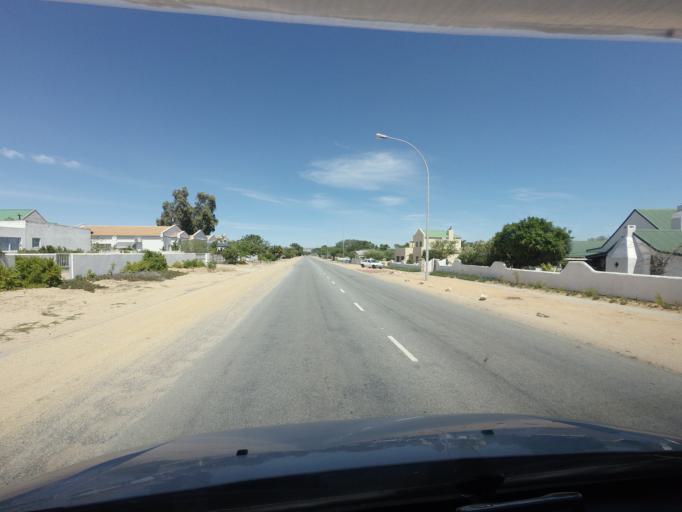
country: ZA
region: Western Cape
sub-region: West Coast District Municipality
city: Vredenburg
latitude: -32.7863
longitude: 18.1860
